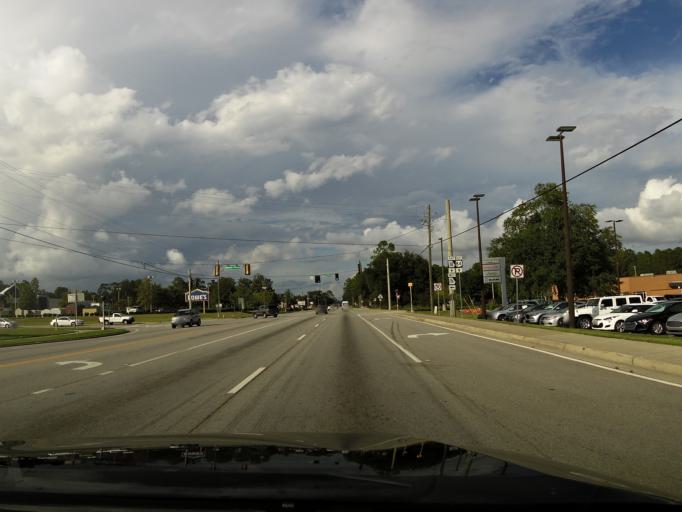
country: US
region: Georgia
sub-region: Liberty County
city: Hinesville
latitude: 31.8263
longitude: -81.5984
